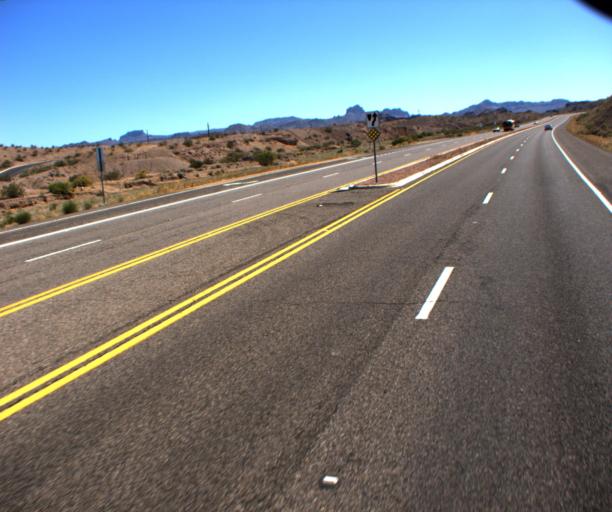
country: US
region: Nevada
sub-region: Clark County
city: Laughlin
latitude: 35.1908
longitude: -114.5254
